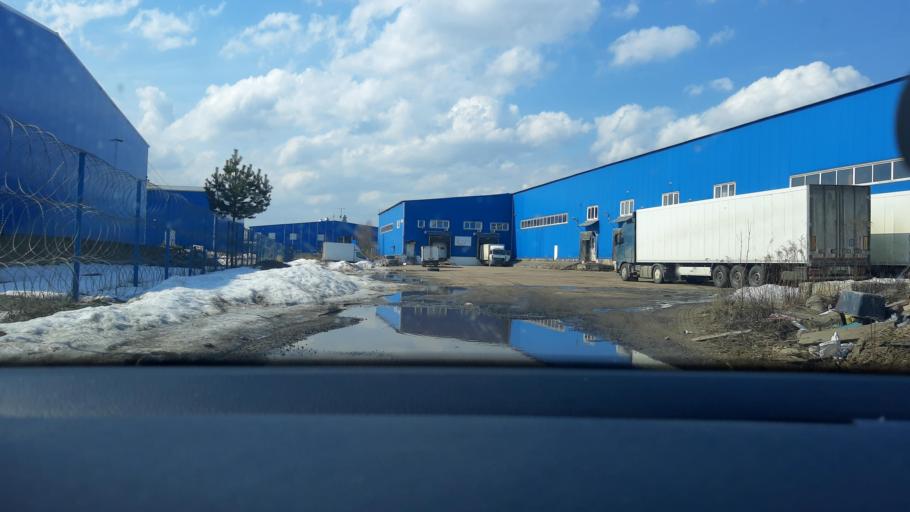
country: RU
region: Moskovskaya
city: Lesnyye Polyany
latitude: 55.9607
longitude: 37.8936
